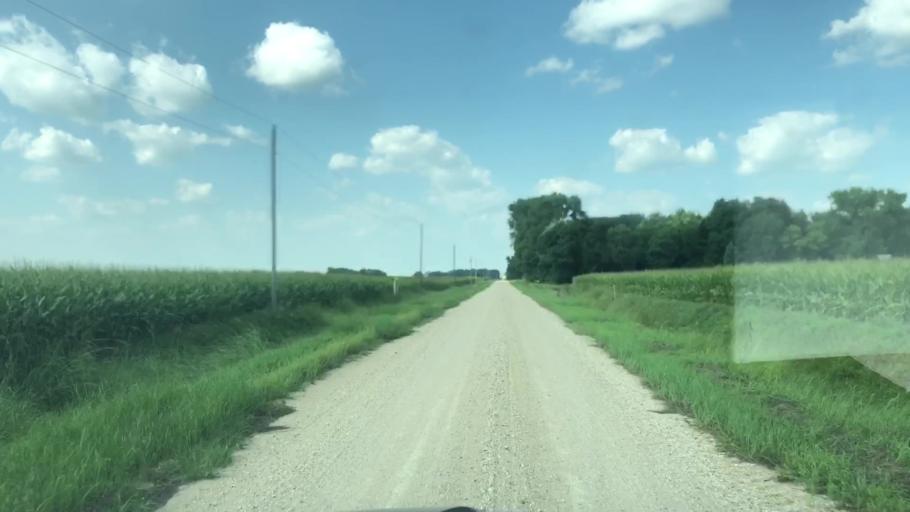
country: US
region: Iowa
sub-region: O'Brien County
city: Sheldon
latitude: 43.1609
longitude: -95.7822
